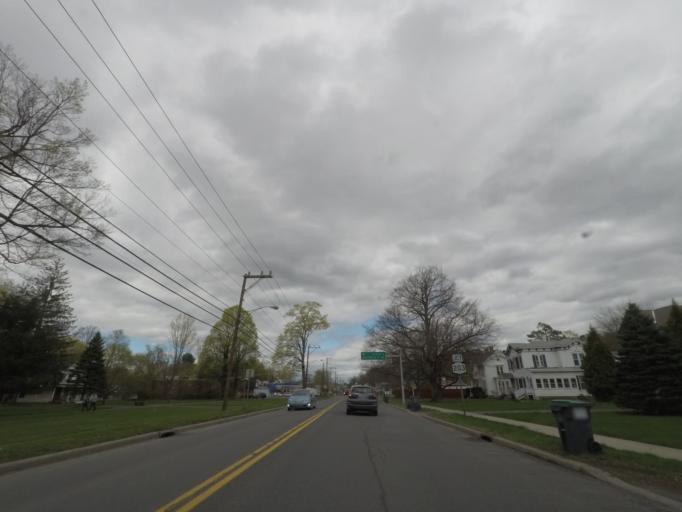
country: US
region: New York
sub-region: Columbia County
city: Chatham
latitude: 42.3551
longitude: -73.6013
